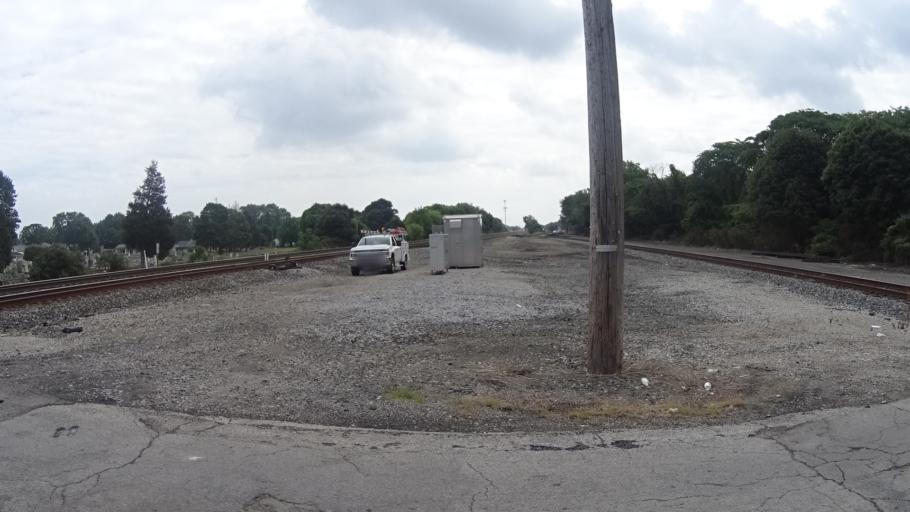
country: US
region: Ohio
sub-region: Erie County
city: Sandusky
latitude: 41.4412
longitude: -82.7275
